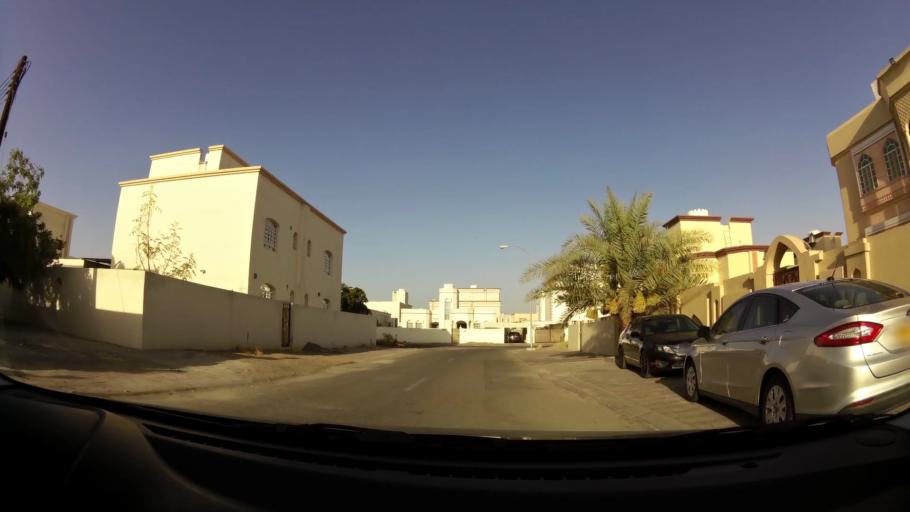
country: OM
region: Muhafazat Masqat
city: As Sib al Jadidah
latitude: 23.6123
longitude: 58.2239
